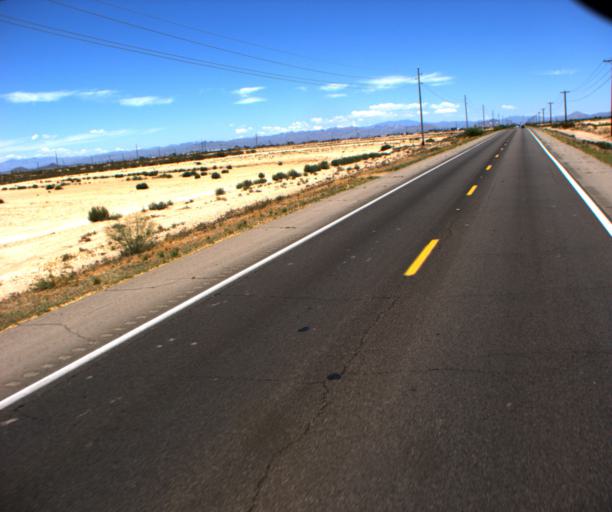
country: US
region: Arizona
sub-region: Pinal County
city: Florence
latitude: 33.0119
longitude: -111.4155
